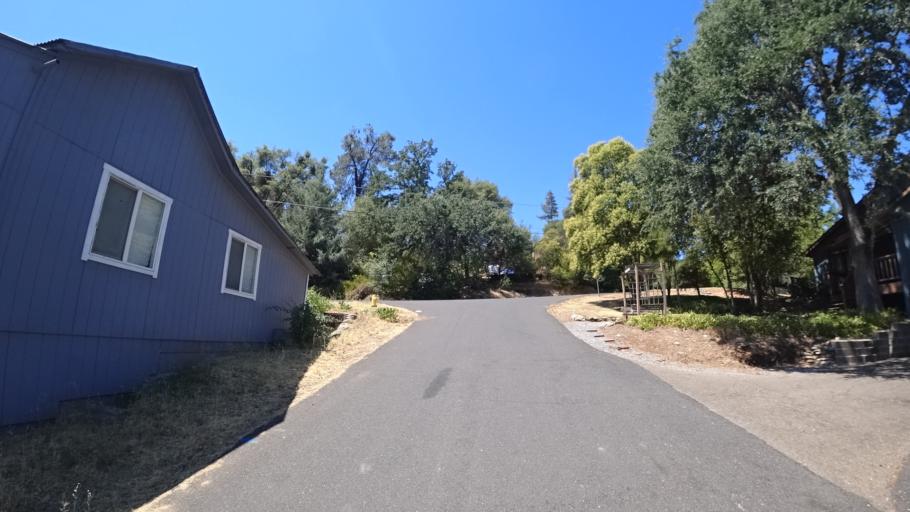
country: US
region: California
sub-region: Calaveras County
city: Angels Camp
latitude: 38.0696
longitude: -120.5428
